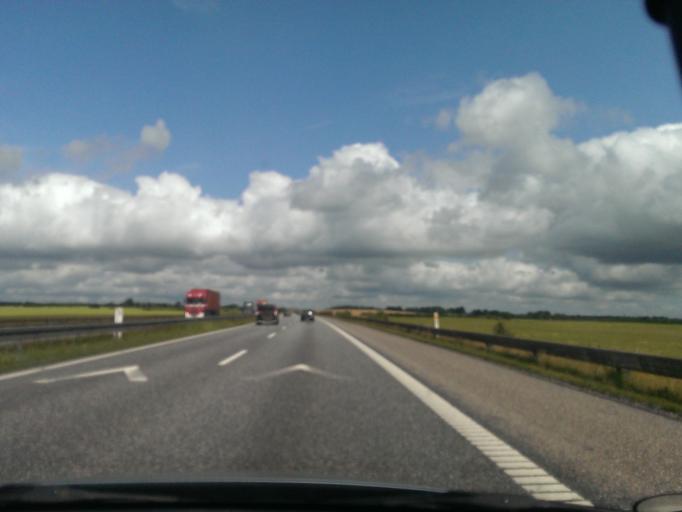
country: DK
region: North Denmark
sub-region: Mariagerfjord Kommune
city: Hobro
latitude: 56.7164
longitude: 9.7245
